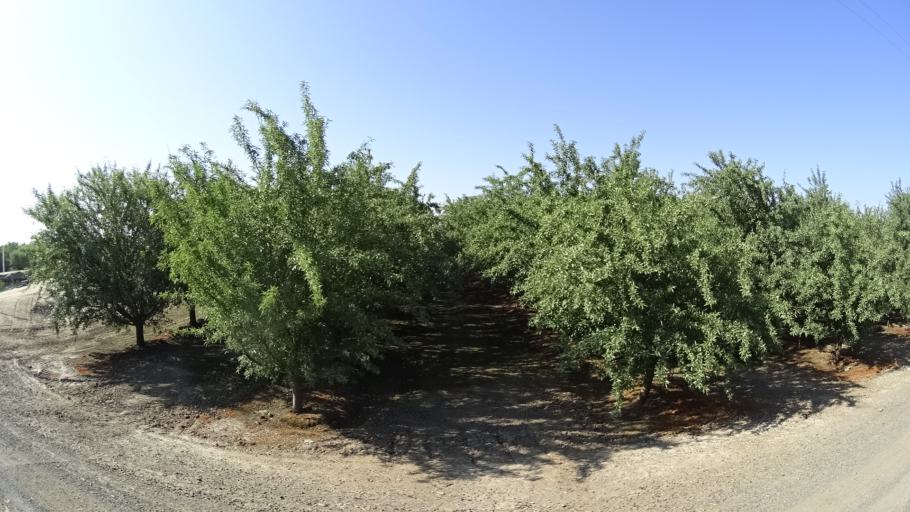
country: US
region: California
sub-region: Kings County
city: Lucerne
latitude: 36.3866
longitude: -119.5760
